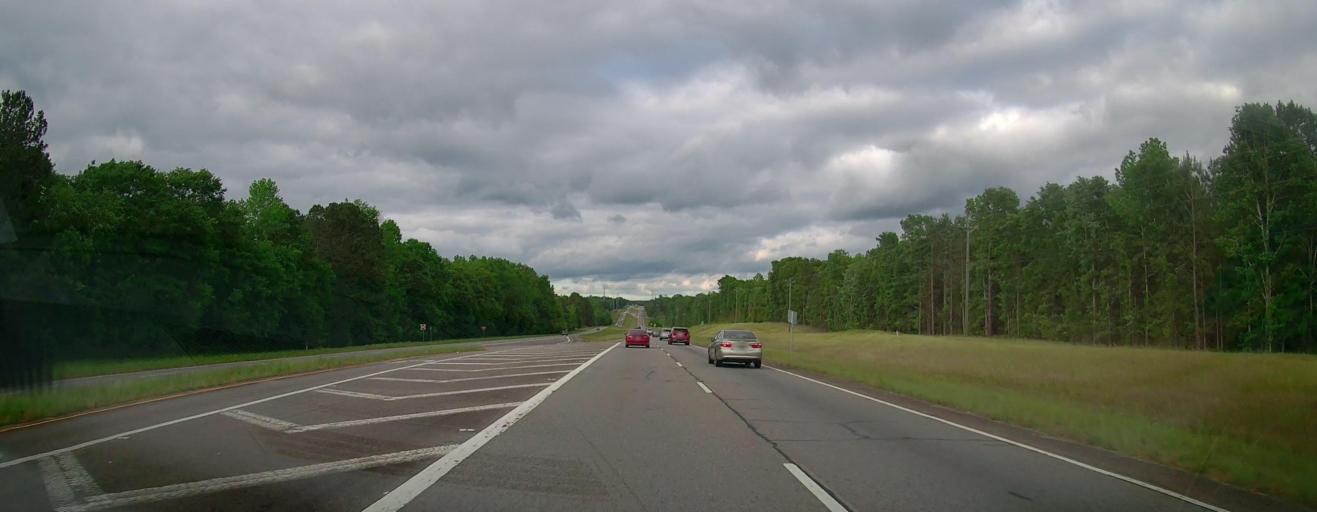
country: US
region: Georgia
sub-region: Oconee County
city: Bogart
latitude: 33.9024
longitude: -83.5710
